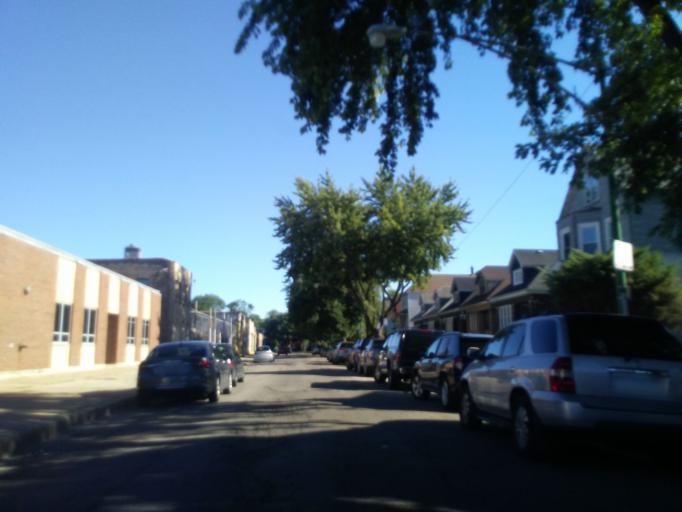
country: US
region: Illinois
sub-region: Cook County
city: Oak Park
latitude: 41.9222
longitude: -87.7426
